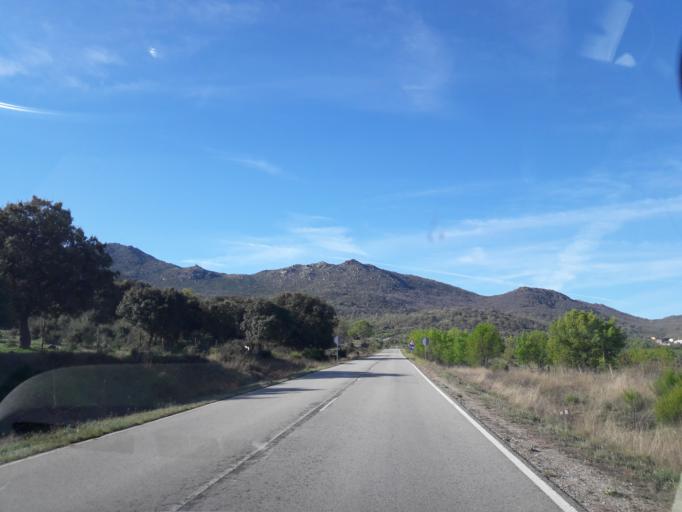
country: ES
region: Castille and Leon
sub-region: Provincia de Salamanca
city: Ledrada
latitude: 40.4518
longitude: -5.7356
